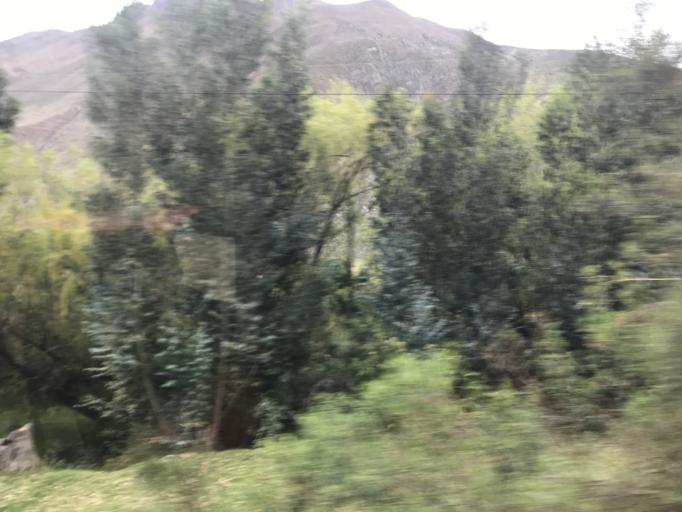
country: PE
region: Cusco
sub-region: Provincia de Urubamba
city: Ollantaytambo
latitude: -13.2431
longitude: -72.2941
